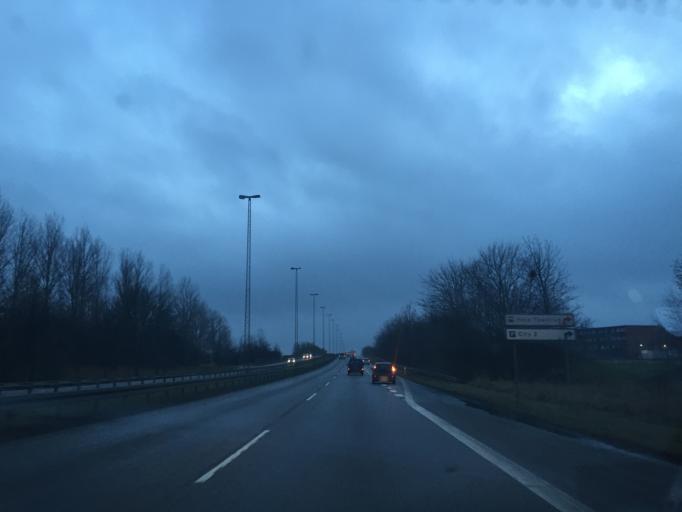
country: DK
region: Capital Region
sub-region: Hoje-Taastrup Kommune
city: Taastrup
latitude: 55.6537
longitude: 12.2824
